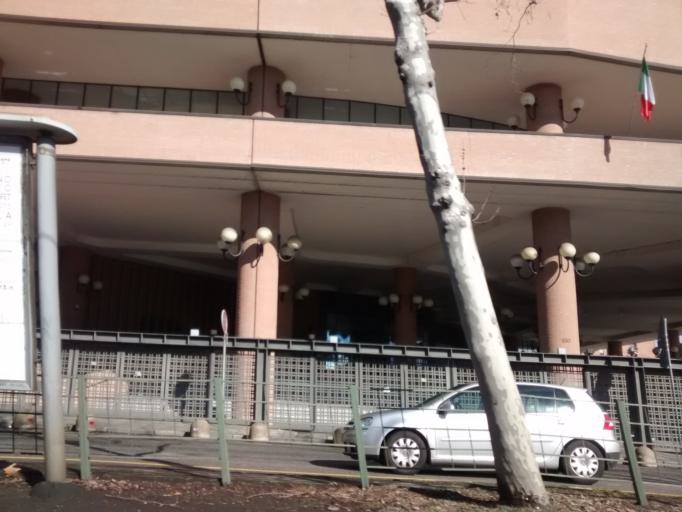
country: IT
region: Piedmont
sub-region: Provincia di Torino
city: Turin
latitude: 45.0699
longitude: 7.6592
